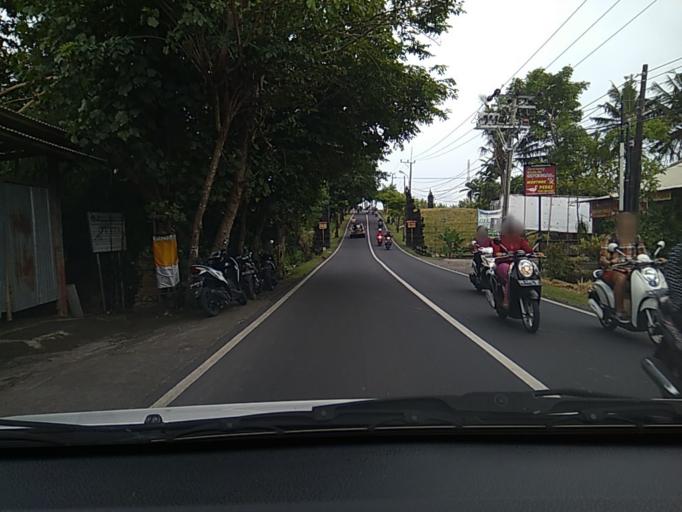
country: ID
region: Bali
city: Banjar Gunungpande
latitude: -8.6355
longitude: 115.1420
